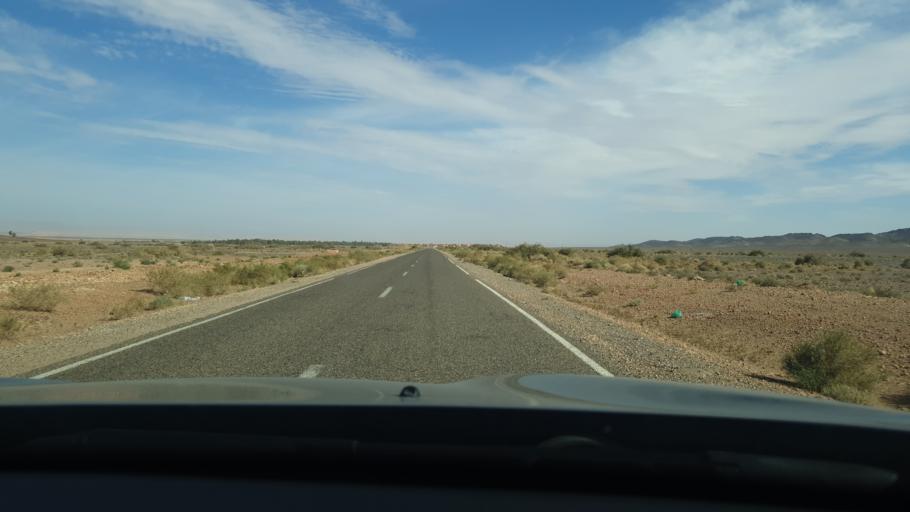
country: MA
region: Meknes-Tafilalet
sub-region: Errachidia
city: Goulmima
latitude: 31.5126
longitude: -4.9867
